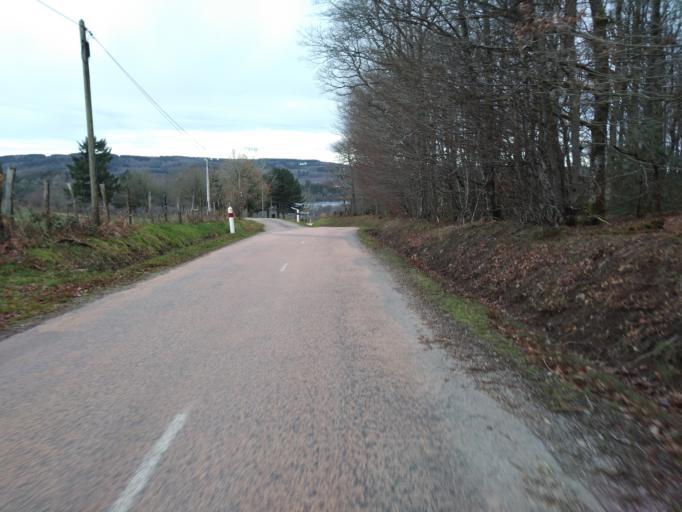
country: FR
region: Bourgogne
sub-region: Departement de la Cote-d'Or
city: Saulieu
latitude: 47.2753
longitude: 4.1592
